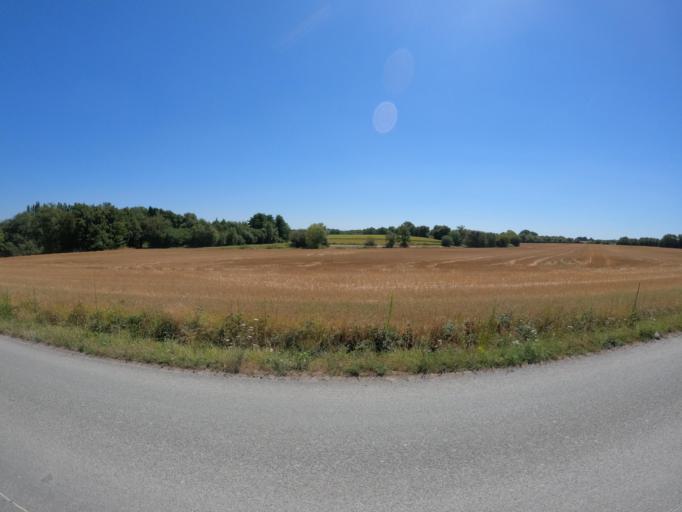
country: FR
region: Pays de la Loire
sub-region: Departement de la Vendee
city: Saint-Philbert-de-Bouaine
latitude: 46.9805
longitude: -1.5361
